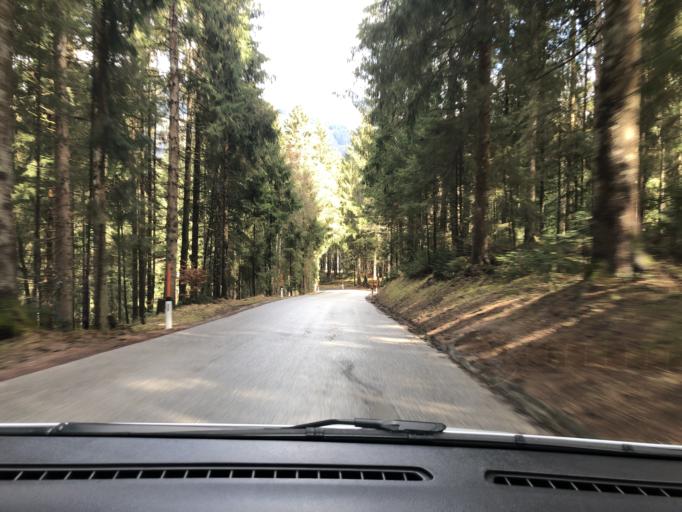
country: AT
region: Tyrol
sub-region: Politischer Bezirk Kitzbuhel
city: Hopfgarten im Brixental
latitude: 47.4472
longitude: 12.1479
